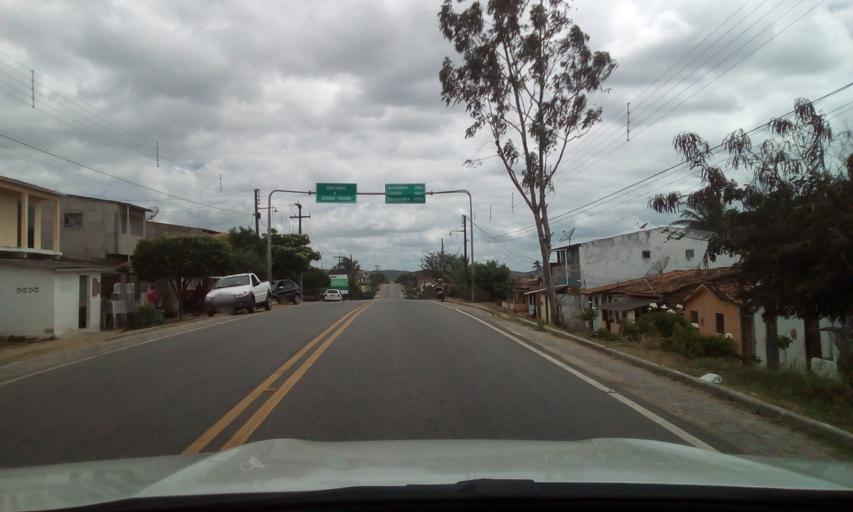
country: BR
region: Paraiba
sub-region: Serra Redonda
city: Alagoa Grande
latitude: -7.1812
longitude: -35.5894
